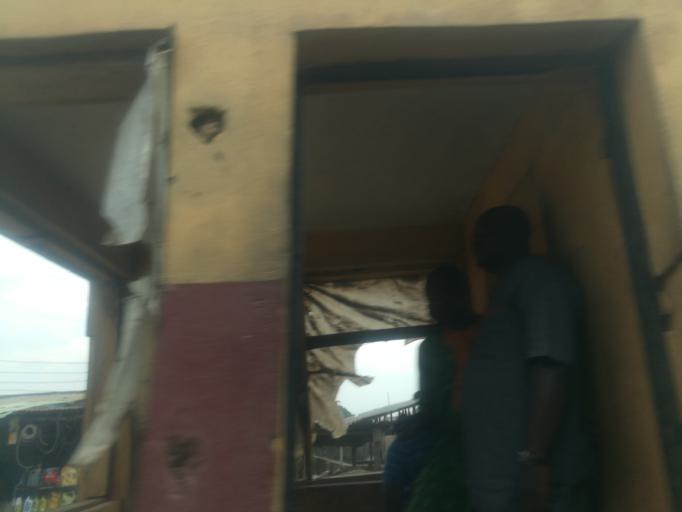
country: NG
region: Oyo
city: Ibadan
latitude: 7.4358
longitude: 3.9192
